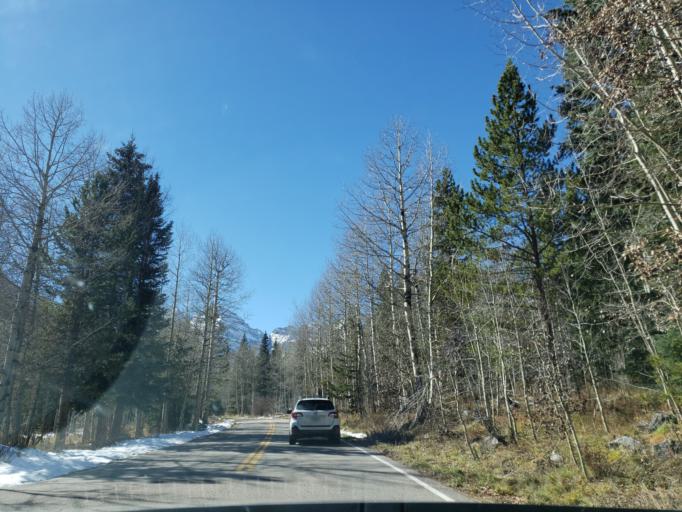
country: US
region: Colorado
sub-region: Pitkin County
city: Snowmass Village
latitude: 39.1007
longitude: -106.9371
